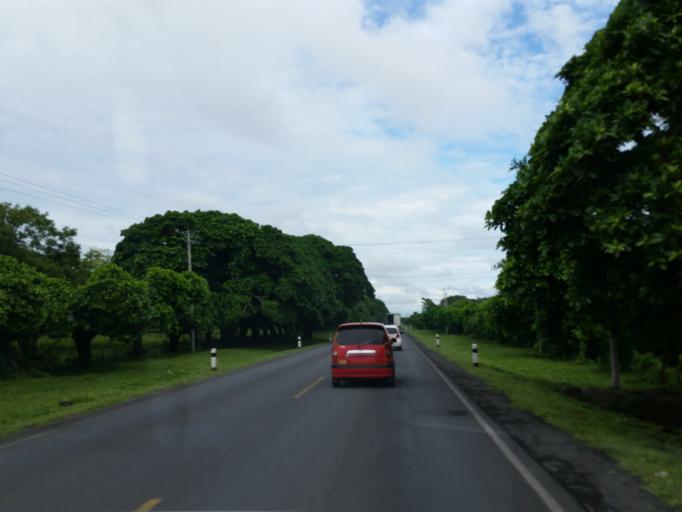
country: NI
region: Leon
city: Nagarote
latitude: 12.2714
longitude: -86.4880
